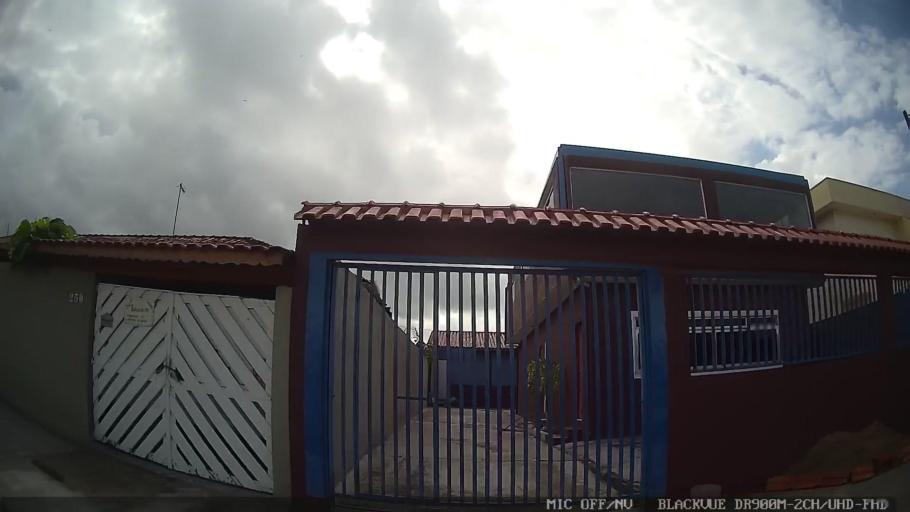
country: BR
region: Sao Paulo
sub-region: Itanhaem
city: Itanhaem
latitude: -24.1974
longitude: -46.8240
